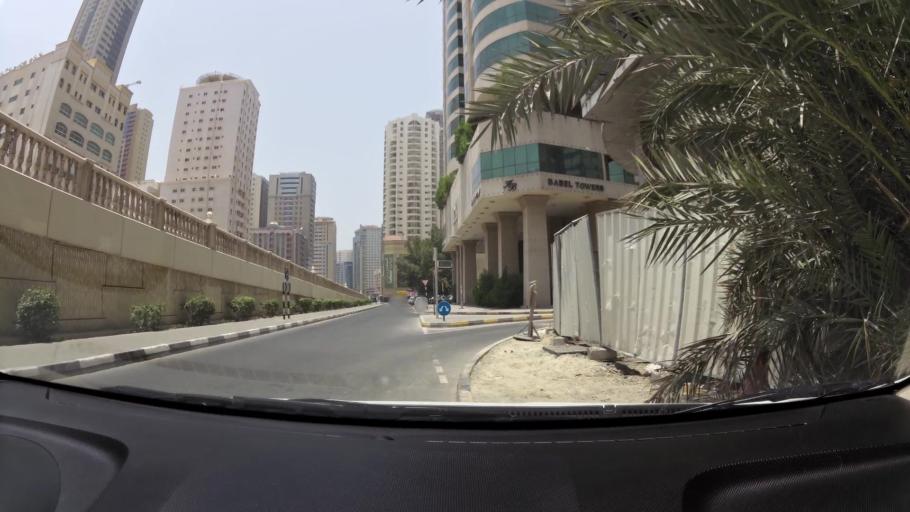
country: AE
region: Ash Shariqah
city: Sharjah
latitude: 25.3241
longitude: 55.3782
